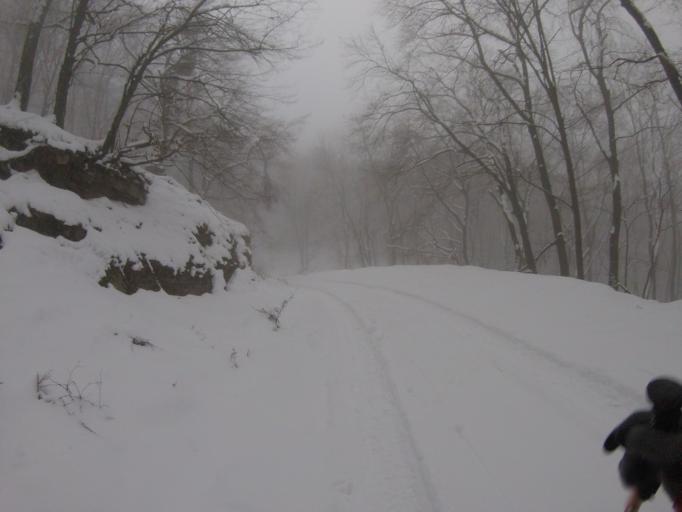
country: HU
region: Heves
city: Szilvasvarad
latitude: 48.0606
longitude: 20.4068
